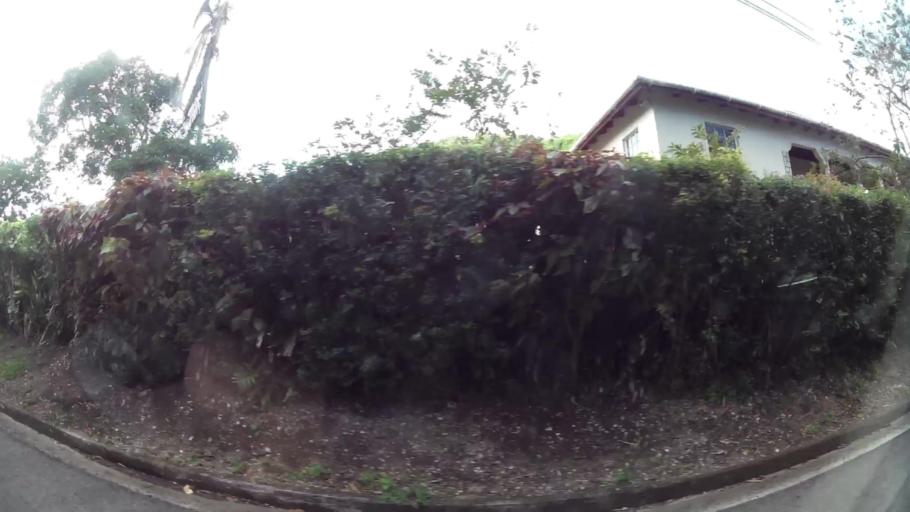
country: AG
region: Saint Peter
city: All Saints
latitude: 17.0417
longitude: -61.8227
